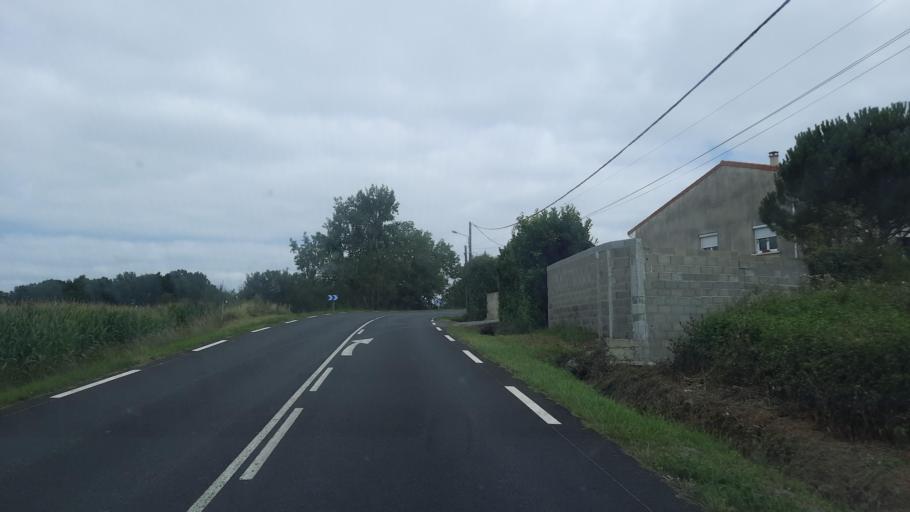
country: FR
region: Midi-Pyrenees
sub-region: Departement des Hautes-Pyrenees
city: Orleix
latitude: 43.2573
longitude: 0.1395
